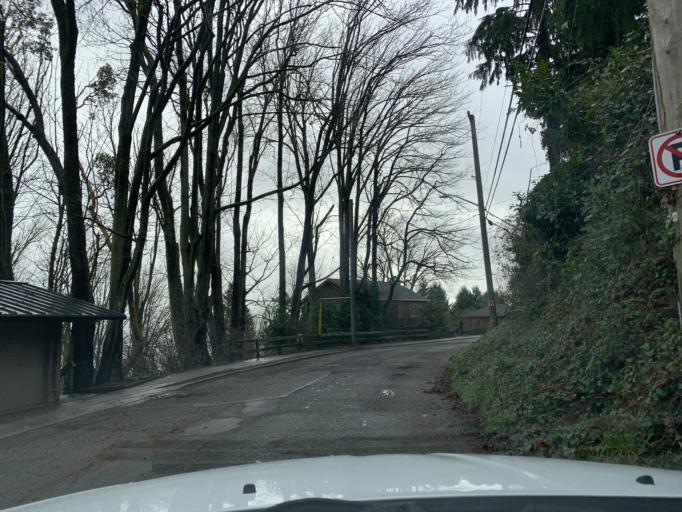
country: US
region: Washington
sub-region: King County
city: Seattle
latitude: 47.6063
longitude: -122.2869
